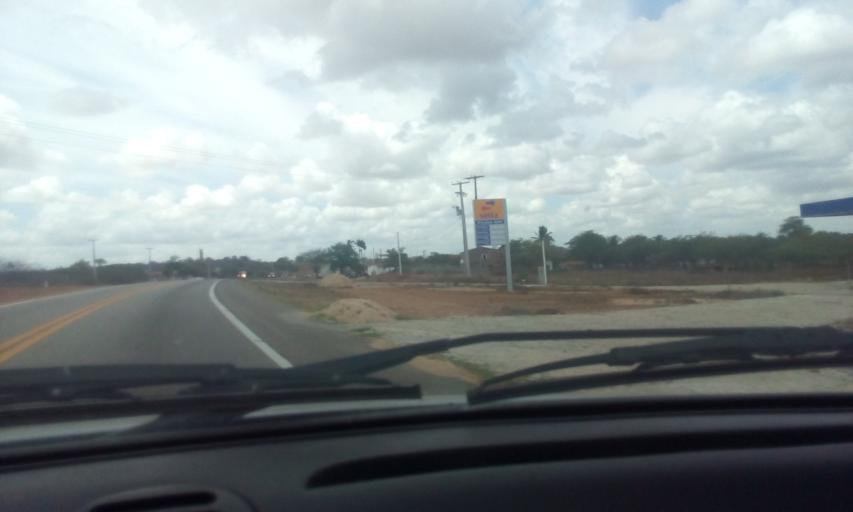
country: BR
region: Rio Grande do Norte
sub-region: Tangara
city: Tangara
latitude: -6.1104
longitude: -35.7113
